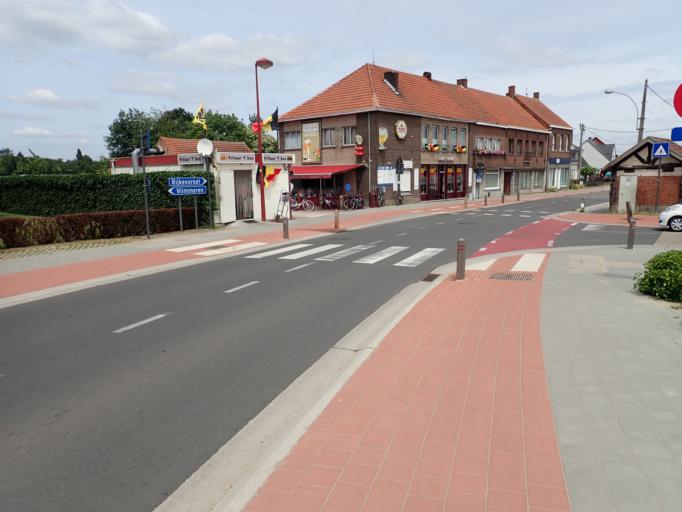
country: BE
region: Flanders
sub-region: Provincie Antwerpen
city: Rijkevorsel
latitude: 51.3298
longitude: 4.7736
